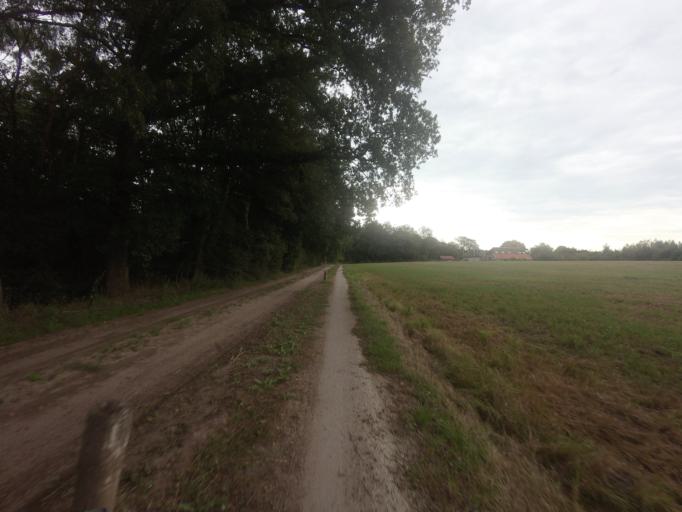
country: NL
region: Overijssel
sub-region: Gemeente Raalte
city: Raalte
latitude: 52.3179
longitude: 6.2894
